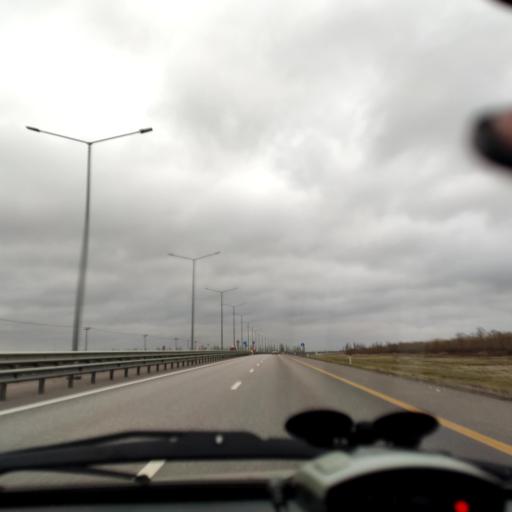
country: RU
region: Voronezj
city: Podkletnoye
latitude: 51.5890
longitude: 39.4284
